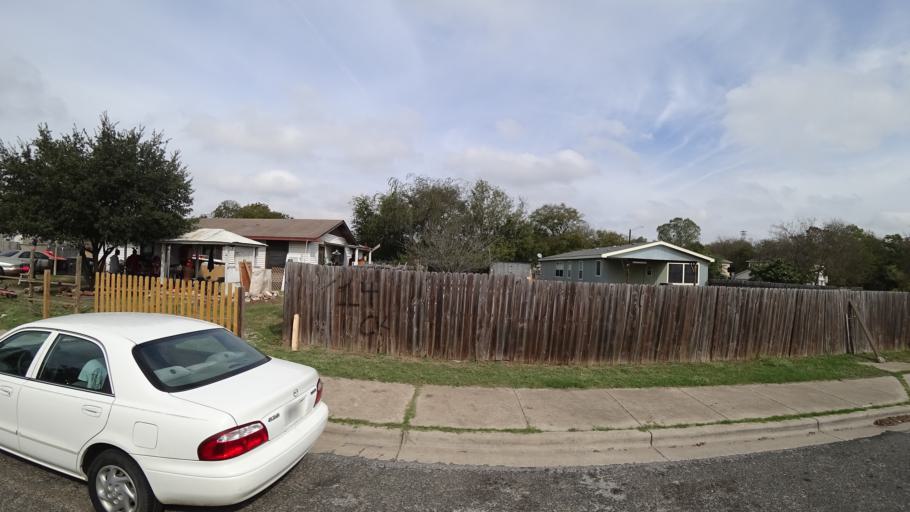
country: US
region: Texas
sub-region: Travis County
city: Wells Branch
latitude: 30.4422
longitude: -97.6603
